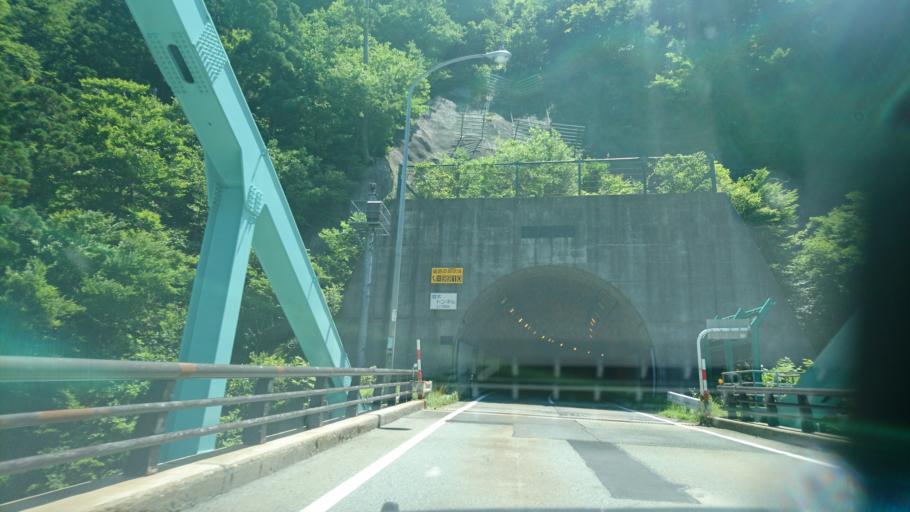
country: JP
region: Iwate
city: Shizukuishi
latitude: 39.6963
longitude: 140.7774
